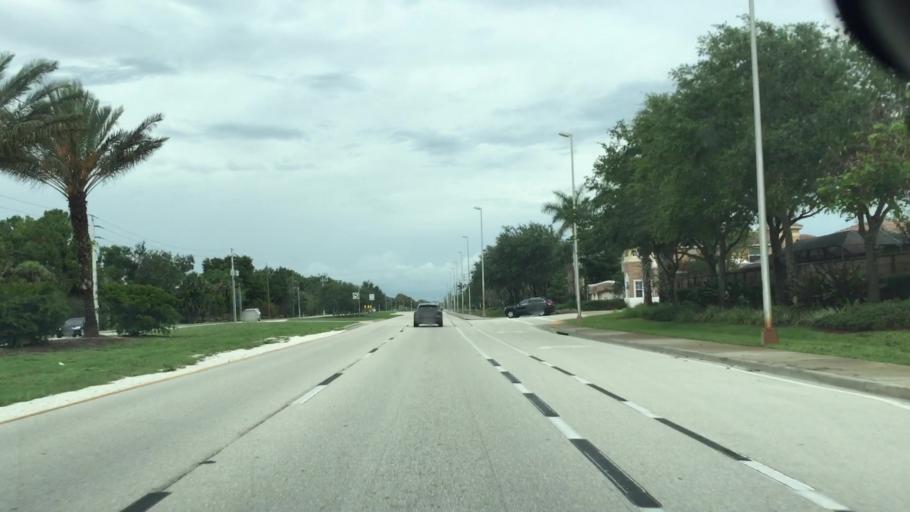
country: US
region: Florida
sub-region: Lee County
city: Estero
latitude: 26.4384
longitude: -81.7885
